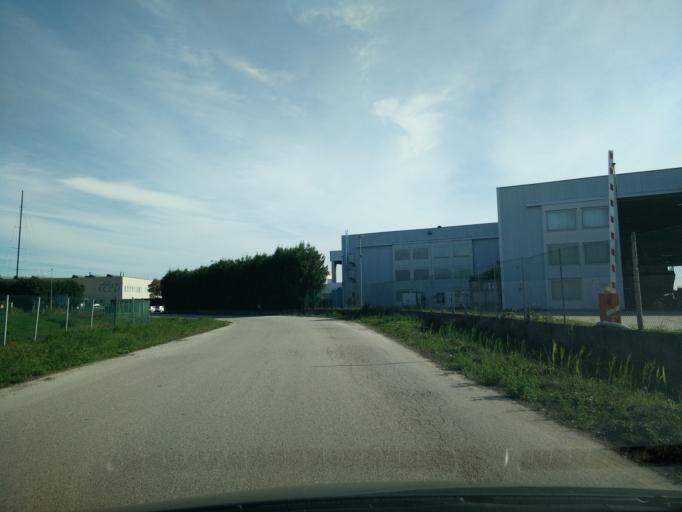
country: IT
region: Veneto
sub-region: Provincia di Venezia
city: Mestre
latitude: 45.4270
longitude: 12.2556
